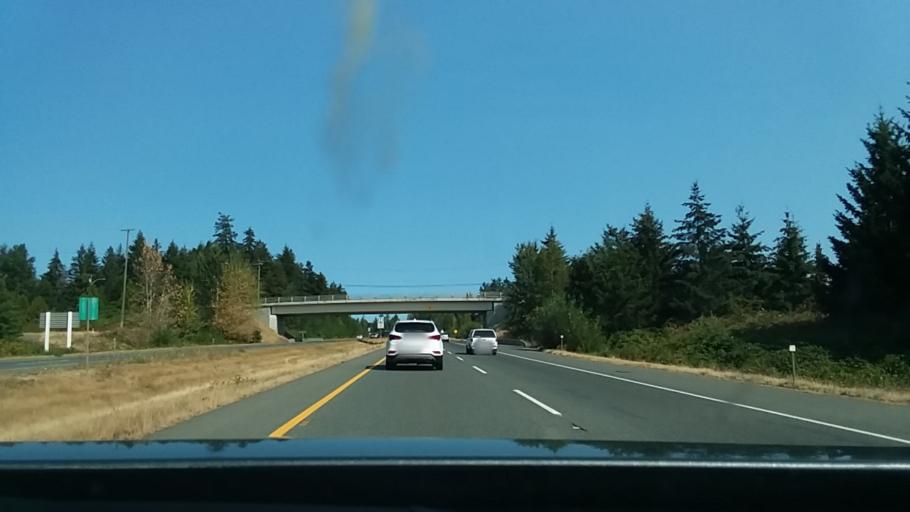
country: CA
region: British Columbia
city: Nanaimo
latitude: 49.1785
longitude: -123.9851
